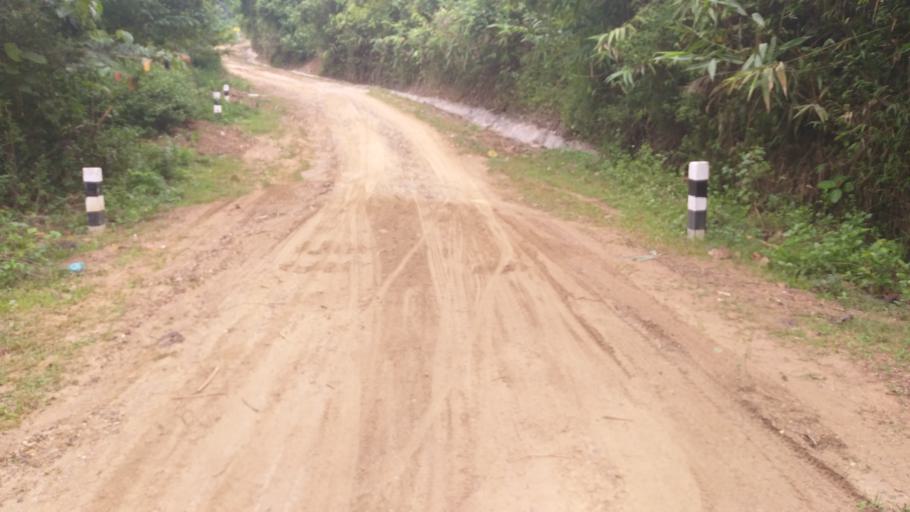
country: LA
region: Phongsali
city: Khoa
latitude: 21.2375
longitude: 102.6709
